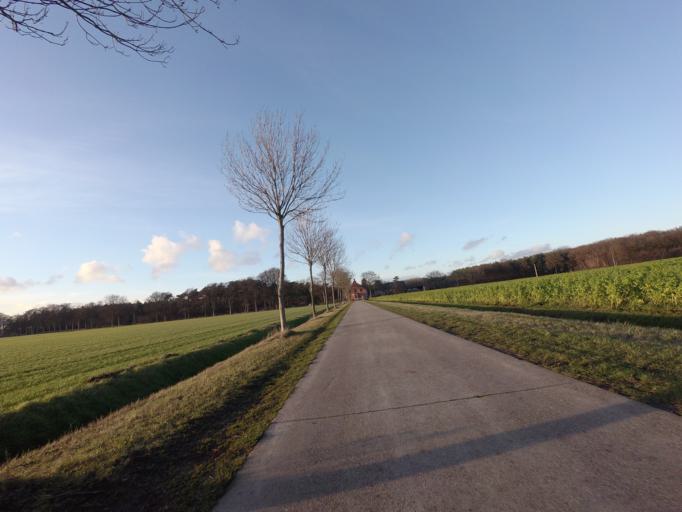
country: BE
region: Flanders
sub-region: Provincie Antwerpen
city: Stabroek
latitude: 51.3501
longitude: 4.3675
